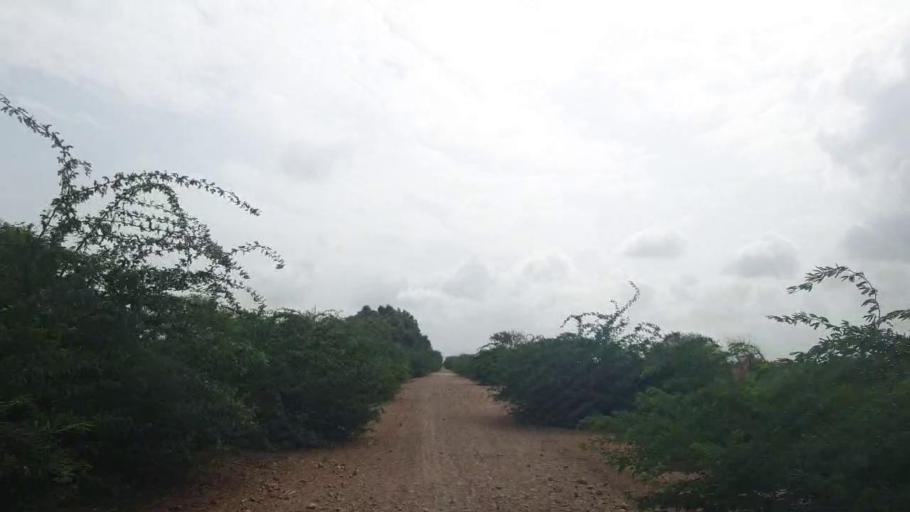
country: PK
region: Sindh
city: Tando Bago
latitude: 24.8201
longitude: 69.0545
